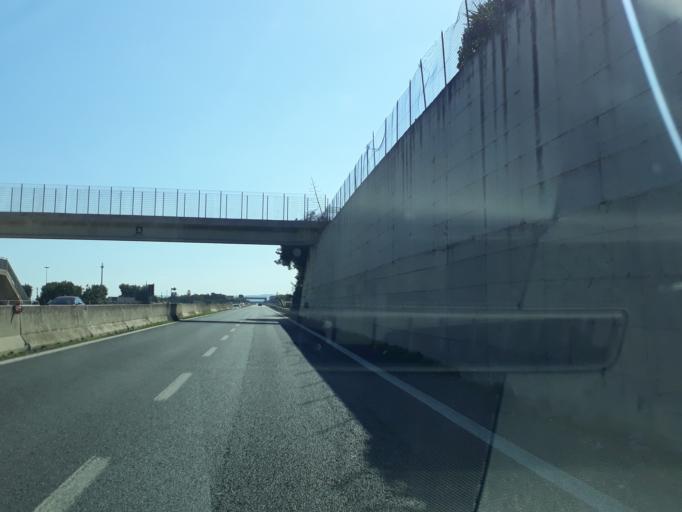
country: IT
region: Apulia
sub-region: Provincia di Brindisi
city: Fasano
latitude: 40.8910
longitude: 17.3326
